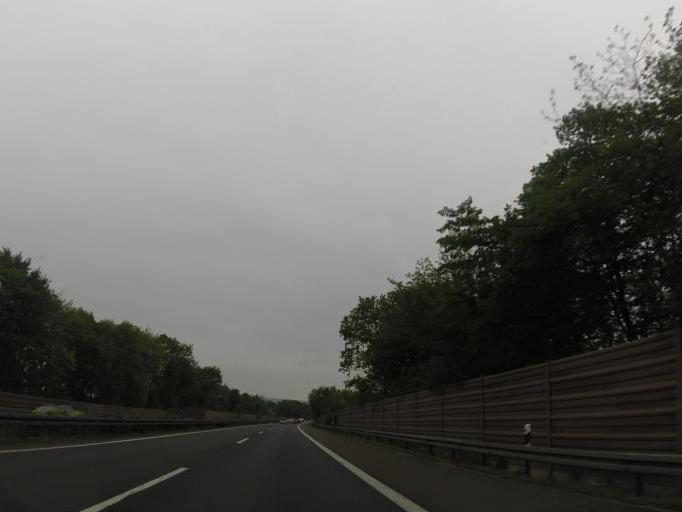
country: DE
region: Lower Saxony
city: Kalefeld
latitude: 51.8174
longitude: 10.1066
